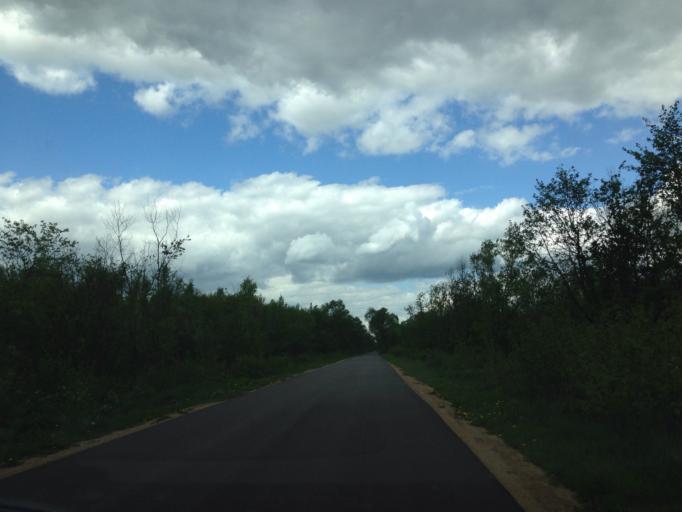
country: PL
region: Podlasie
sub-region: Powiat bialostocki
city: Tykocin
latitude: 53.3087
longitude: 22.6034
